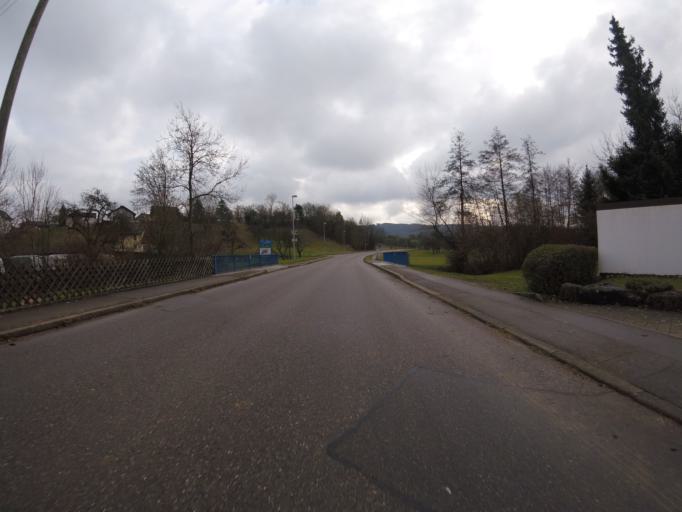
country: DE
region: Baden-Wuerttemberg
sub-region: Regierungsbezirk Stuttgart
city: Allmersbach im Tal
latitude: 48.9171
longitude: 9.4844
